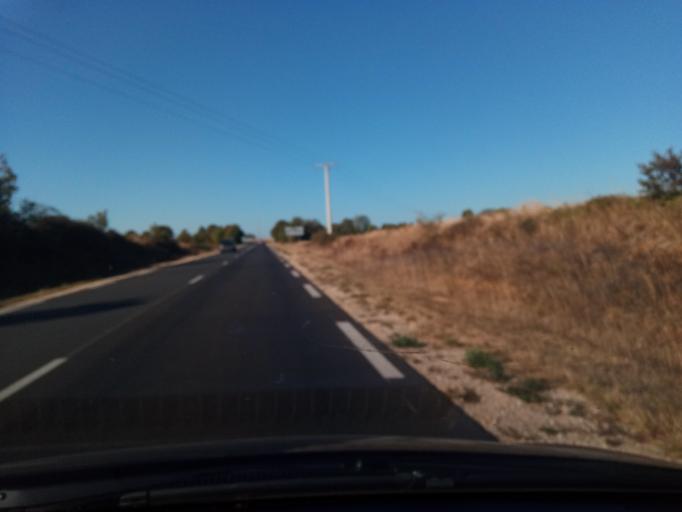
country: FR
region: Poitou-Charentes
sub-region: Departement de la Vienne
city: Lussac-les-Chateaux
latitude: 46.3977
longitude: 0.7359
